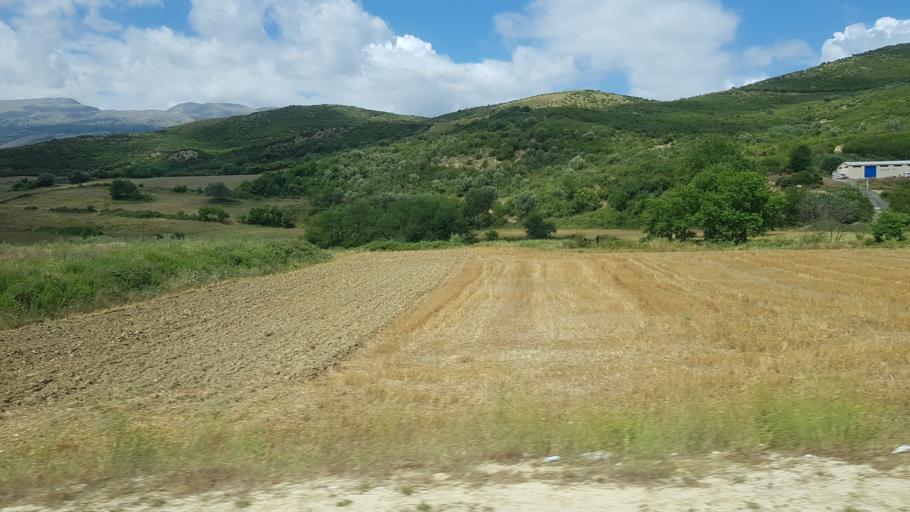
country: AL
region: Gjirokaster
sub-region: Rrethi i Tepelenes
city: Krahes
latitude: 40.4093
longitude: 19.8598
